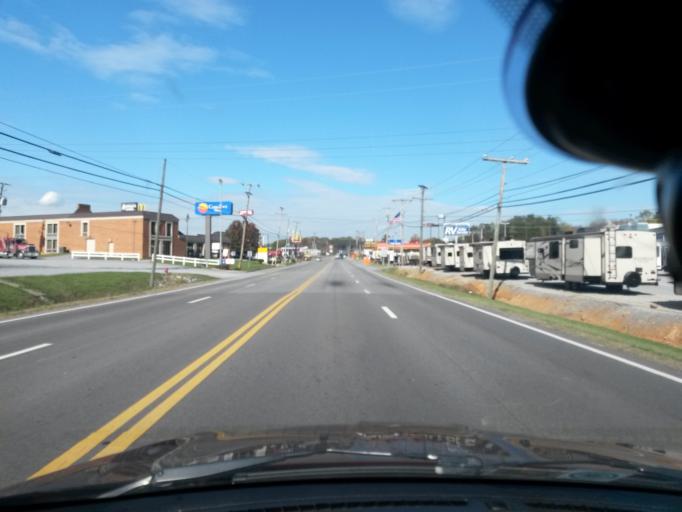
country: US
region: Virginia
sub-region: Botetourt County
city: Cloverdale
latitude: 37.3827
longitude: -79.9029
